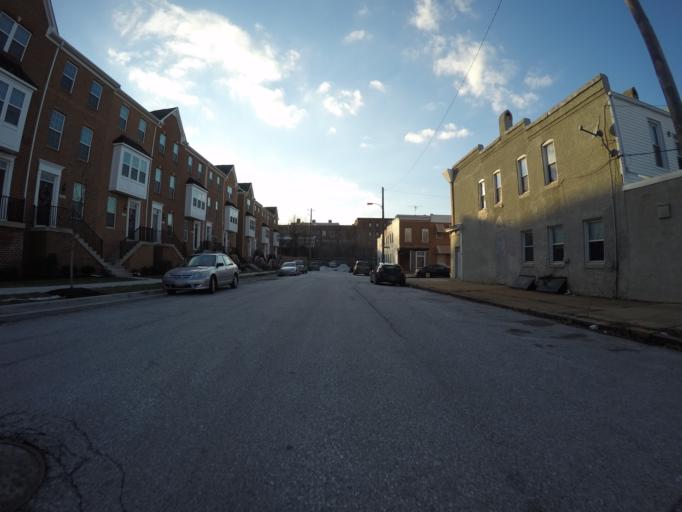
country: US
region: Maryland
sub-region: Baltimore County
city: Dundalk
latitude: 39.2850
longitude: -76.5575
